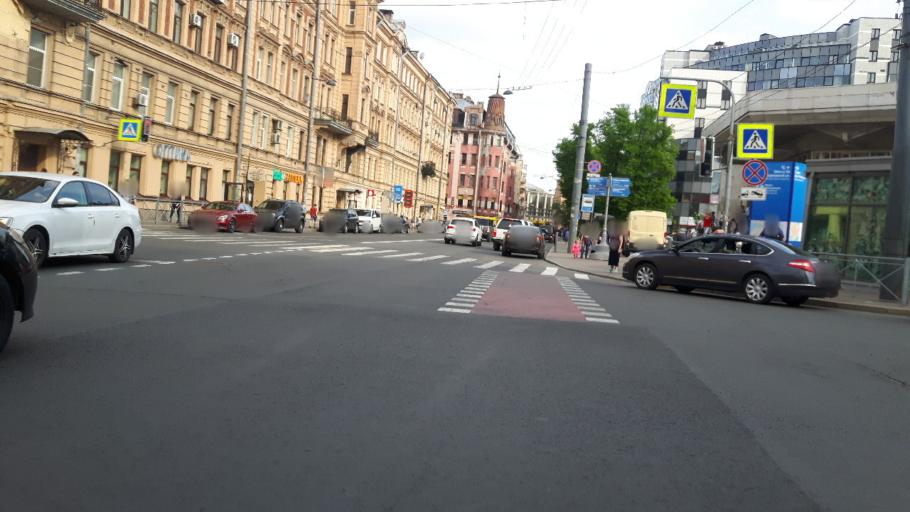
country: RU
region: St.-Petersburg
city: Petrogradka
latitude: 59.9615
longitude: 30.2916
